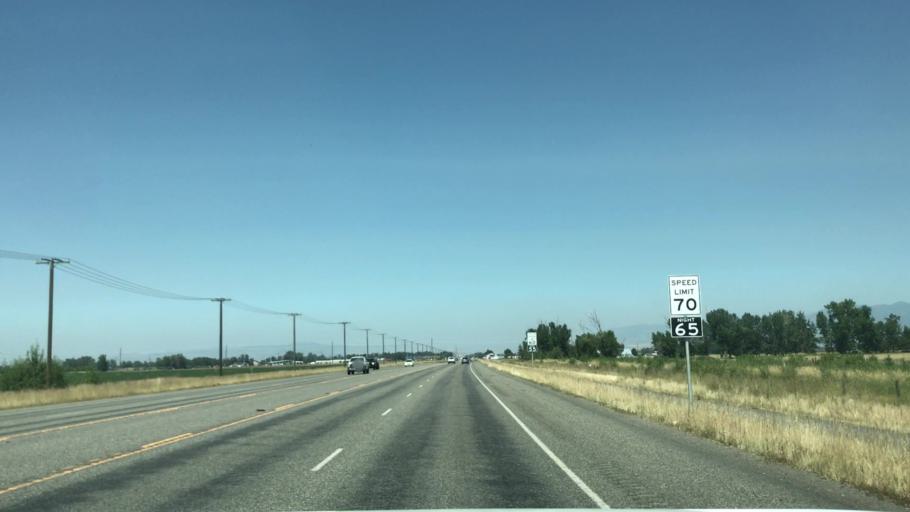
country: US
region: Montana
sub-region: Gallatin County
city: Four Corners
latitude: 45.6857
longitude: -111.1858
